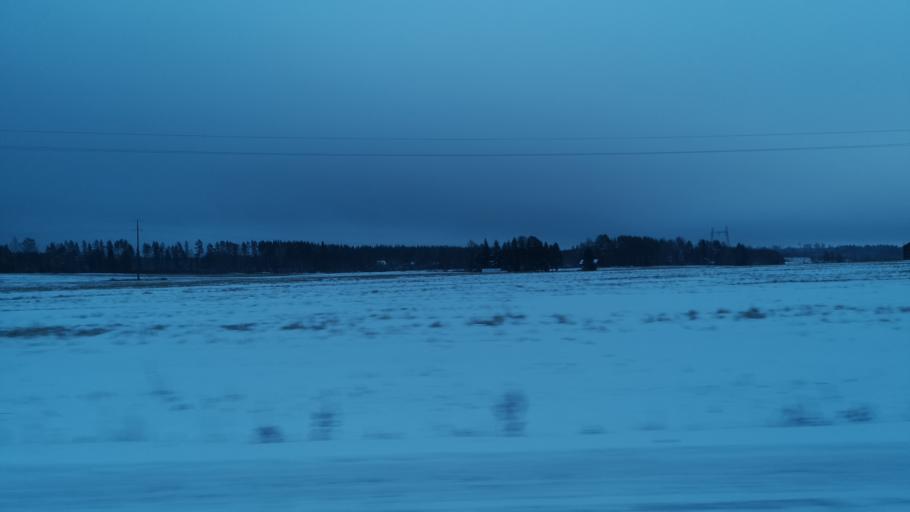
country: FI
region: Southern Savonia
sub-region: Savonlinna
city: Savonlinna
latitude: 61.9623
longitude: 28.8292
